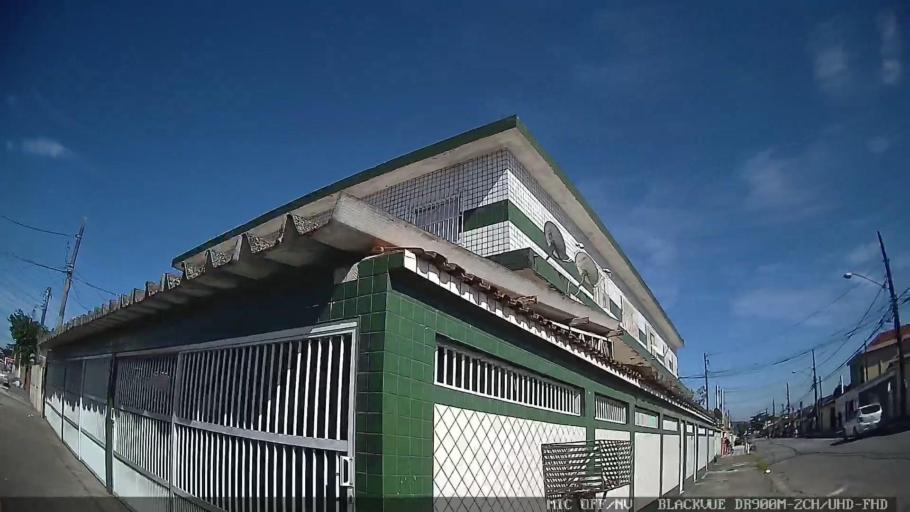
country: BR
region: Sao Paulo
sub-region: Santos
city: Santos
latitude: -23.9445
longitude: -46.2947
